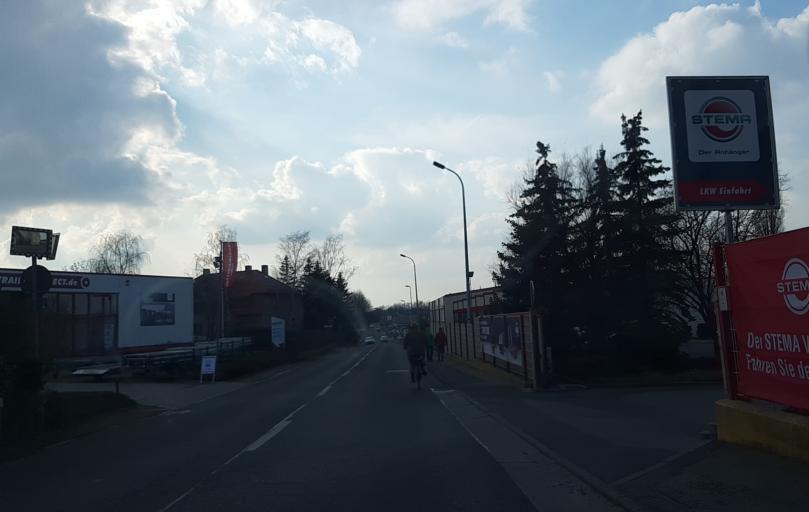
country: DE
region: Saxony
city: Wildenhain
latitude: 51.2885
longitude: 13.4983
